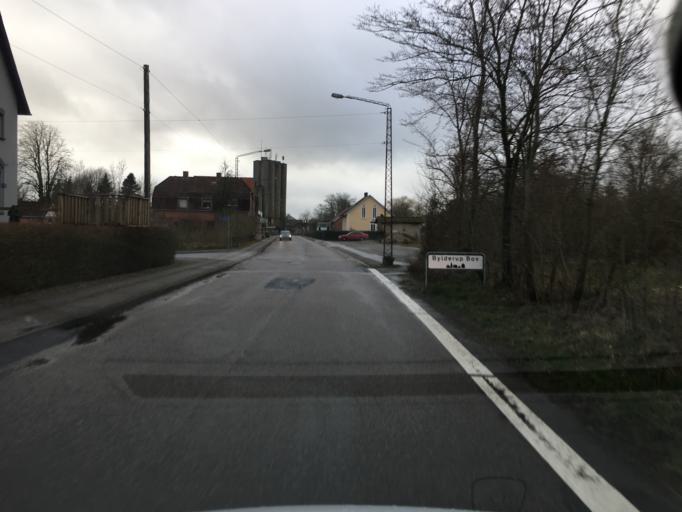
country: DE
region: Schleswig-Holstein
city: Bramstedtlund
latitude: 54.9424
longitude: 9.0905
